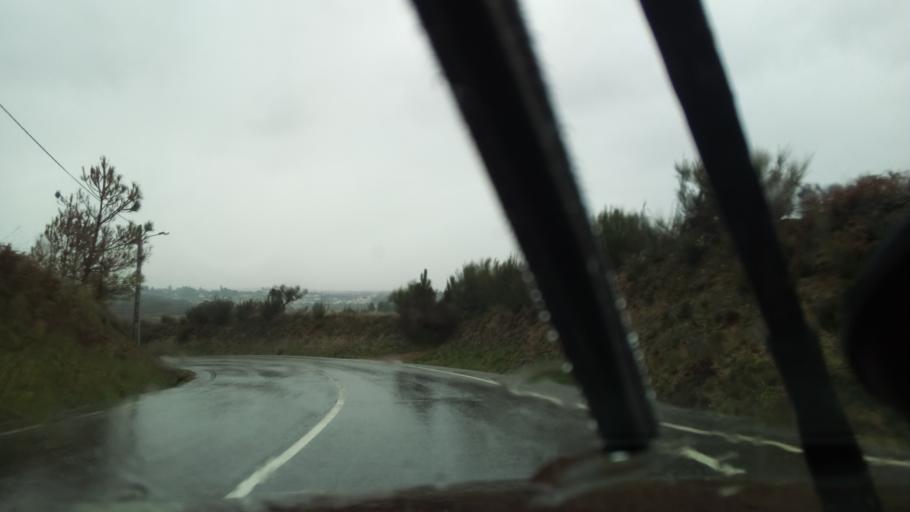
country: PT
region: Guarda
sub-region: Manteigas
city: Manteigas
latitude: 40.5058
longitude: -7.5859
